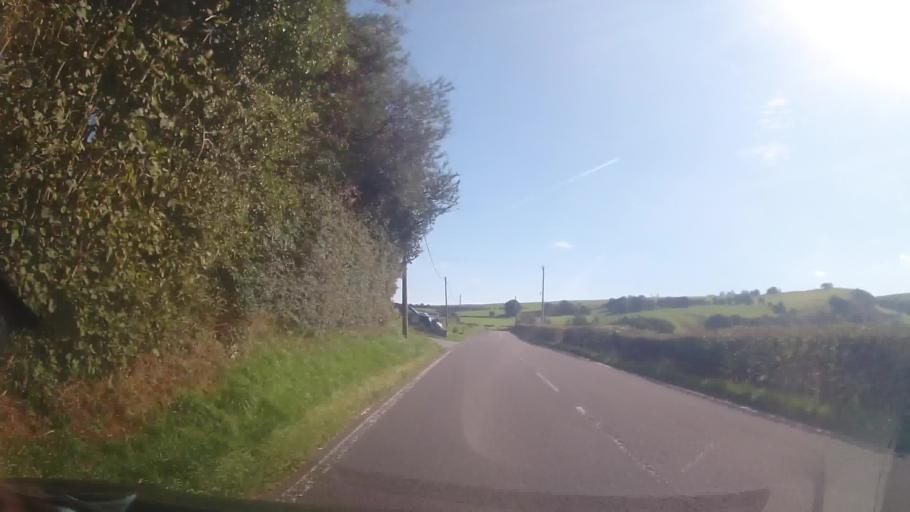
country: GB
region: Wales
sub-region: Sir Powys
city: Mochdre
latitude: 52.4765
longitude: -3.3221
